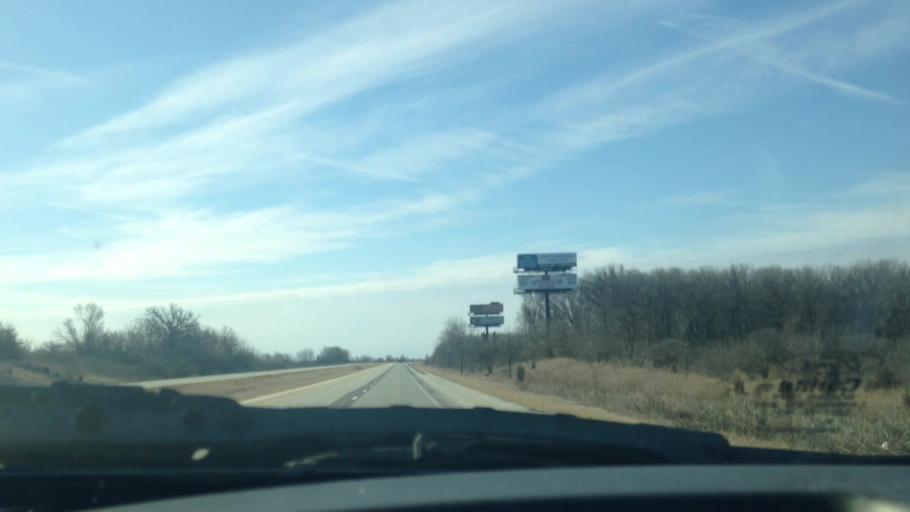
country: US
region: Illinois
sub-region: Ford County
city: Paxton
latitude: 40.5156
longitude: -88.0848
